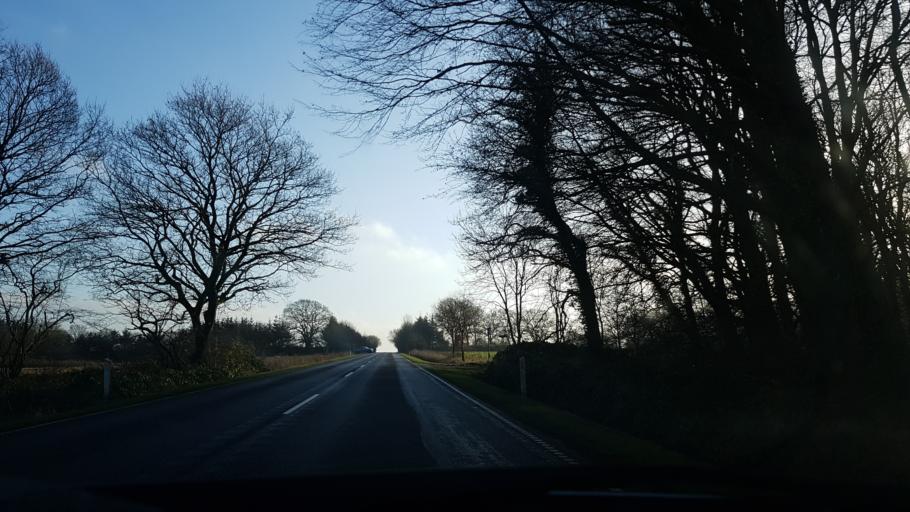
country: DK
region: South Denmark
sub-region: Tonder Kommune
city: Toftlund
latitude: 55.2204
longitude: 9.1792
